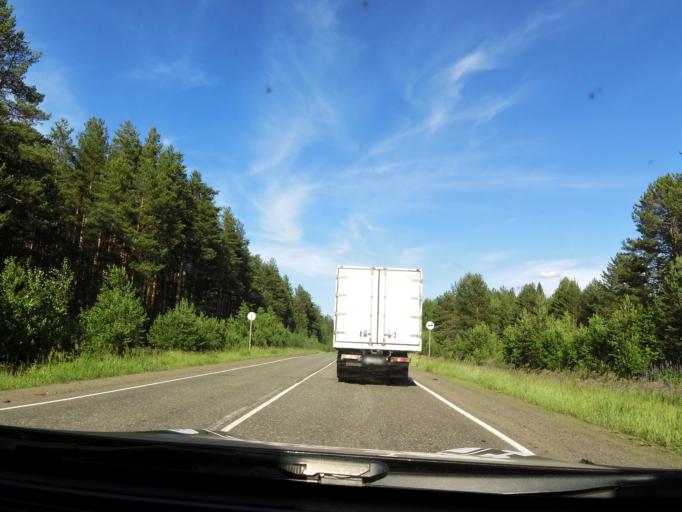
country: RU
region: Kirov
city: Dubrovka
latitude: 58.9057
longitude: 51.2187
